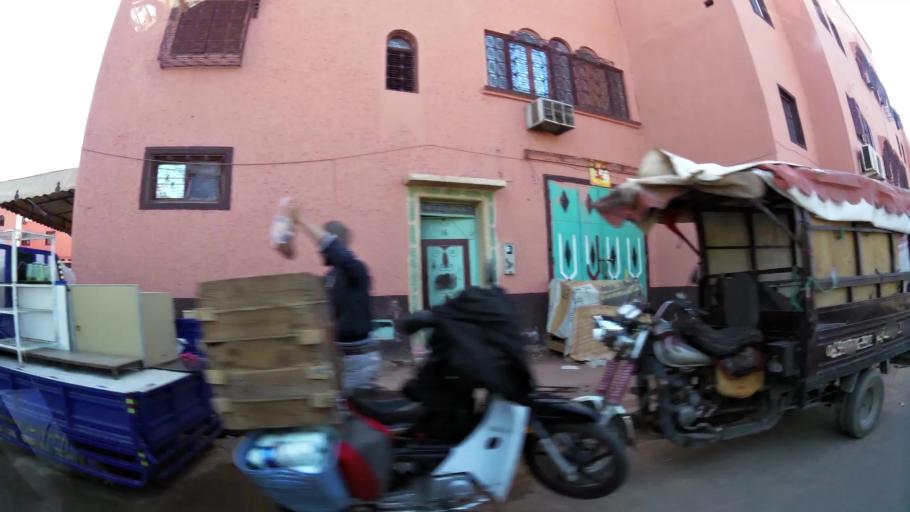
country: MA
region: Marrakech-Tensift-Al Haouz
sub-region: Marrakech
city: Marrakesh
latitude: 31.6514
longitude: -8.0242
